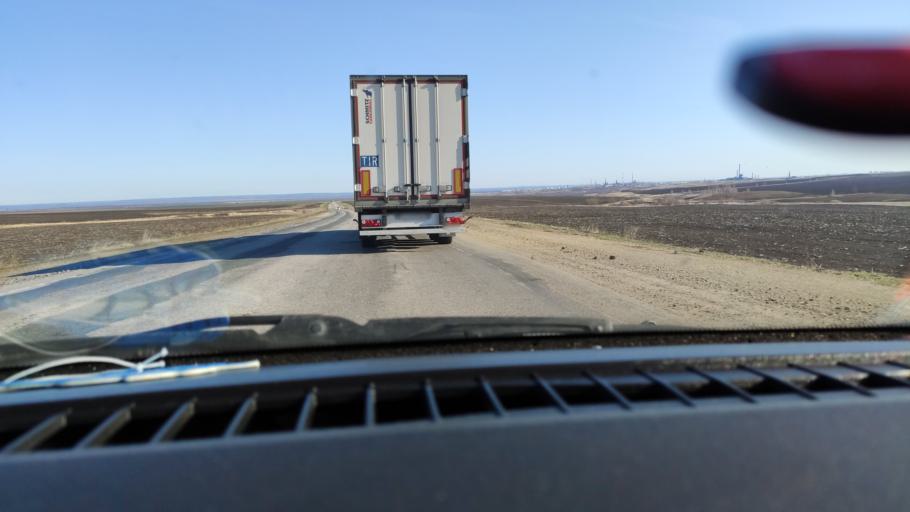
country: RU
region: Samara
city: Syzran'
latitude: 53.0072
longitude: 48.3321
